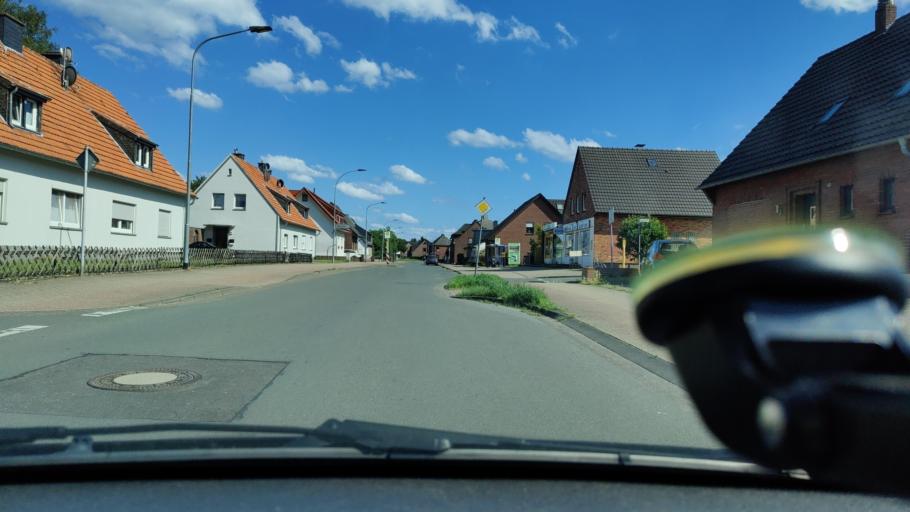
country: DE
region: North Rhine-Westphalia
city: Rheinberg
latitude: 51.5551
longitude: 6.5523
